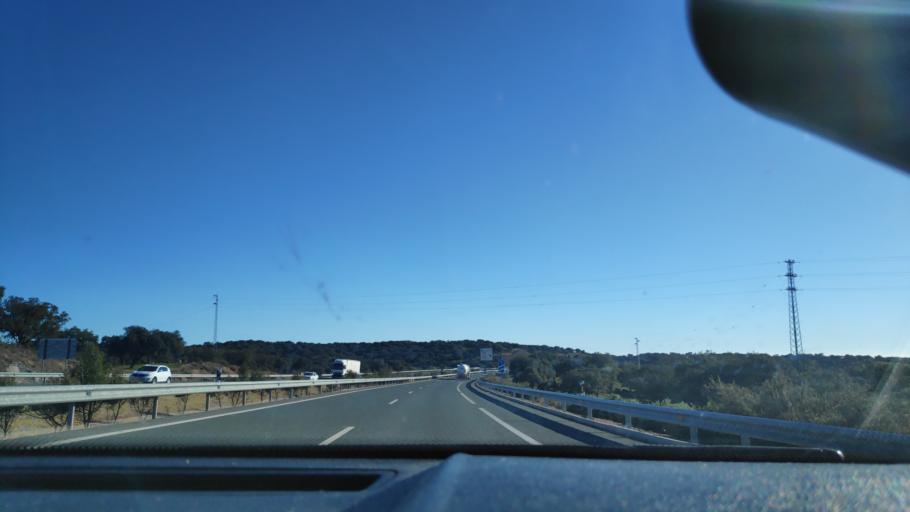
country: ES
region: Andalusia
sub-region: Provincia de Huelva
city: Santa Olalla del Cala
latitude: 37.9090
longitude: -6.2145
